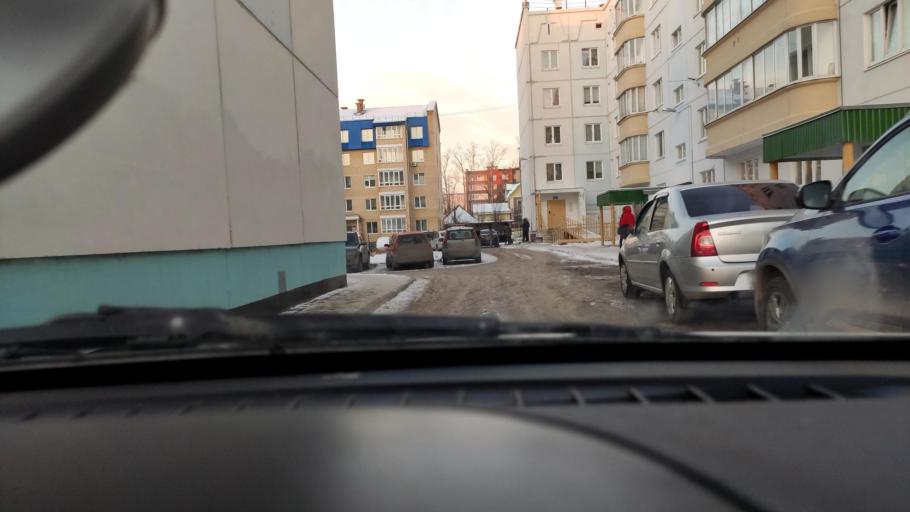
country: RU
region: Perm
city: Perm
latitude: 58.1189
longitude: 56.3795
